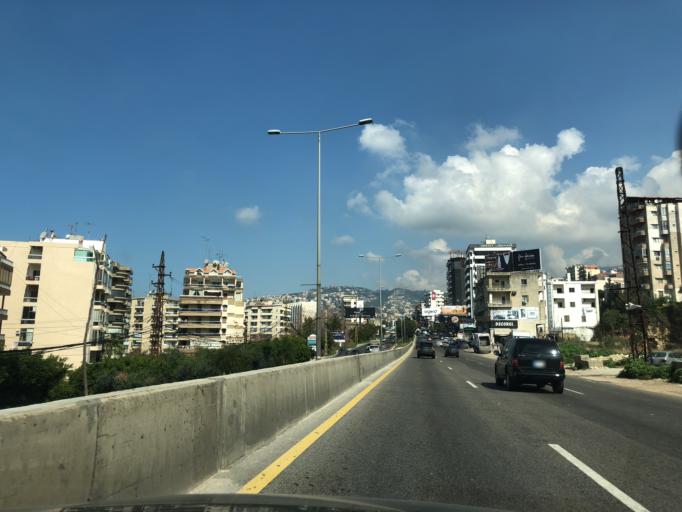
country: LB
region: Mont-Liban
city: Djounie
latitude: 33.9911
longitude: 35.6430
